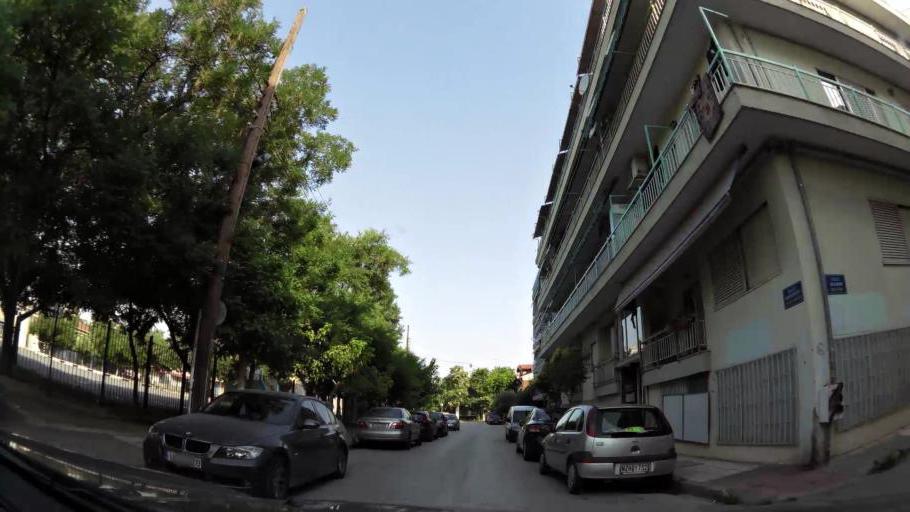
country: GR
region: Central Macedonia
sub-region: Nomos Thessalonikis
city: Menemeni
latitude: 40.6572
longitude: 22.9100
